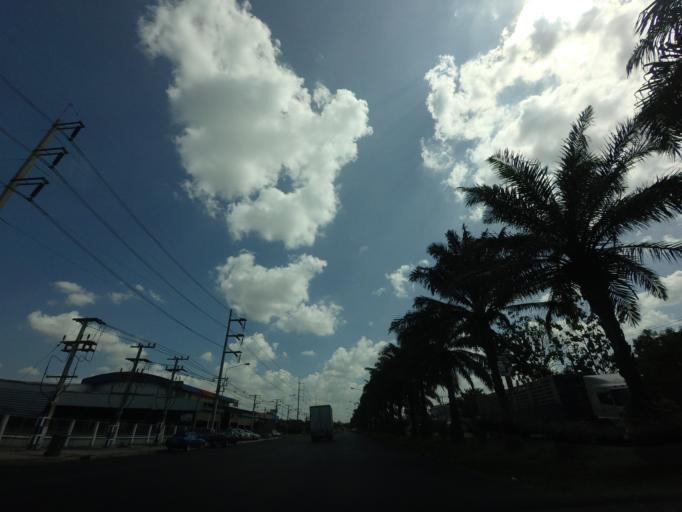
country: TH
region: Chon Buri
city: Ban Bueng
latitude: 13.3084
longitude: 101.1083
